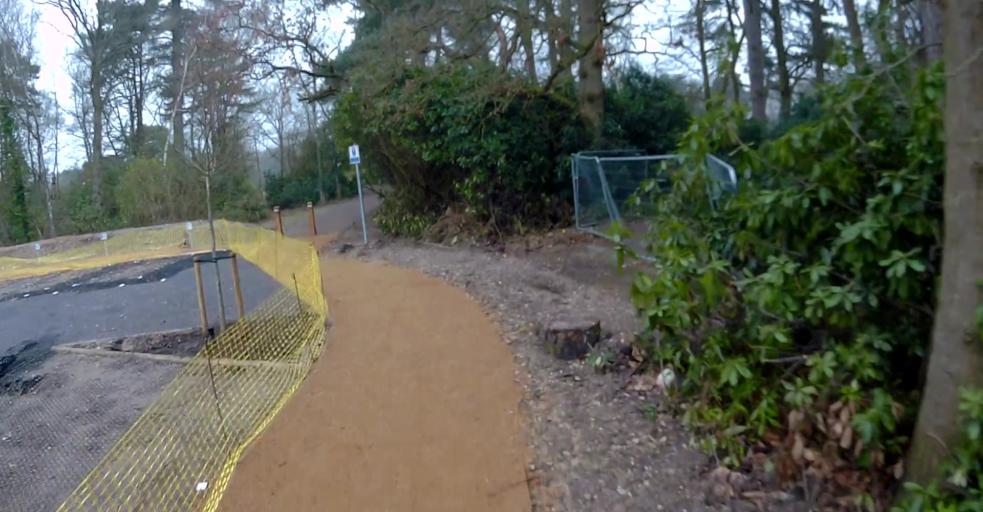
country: GB
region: England
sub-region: Wokingham
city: Barkham
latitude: 51.3783
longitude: -0.8728
